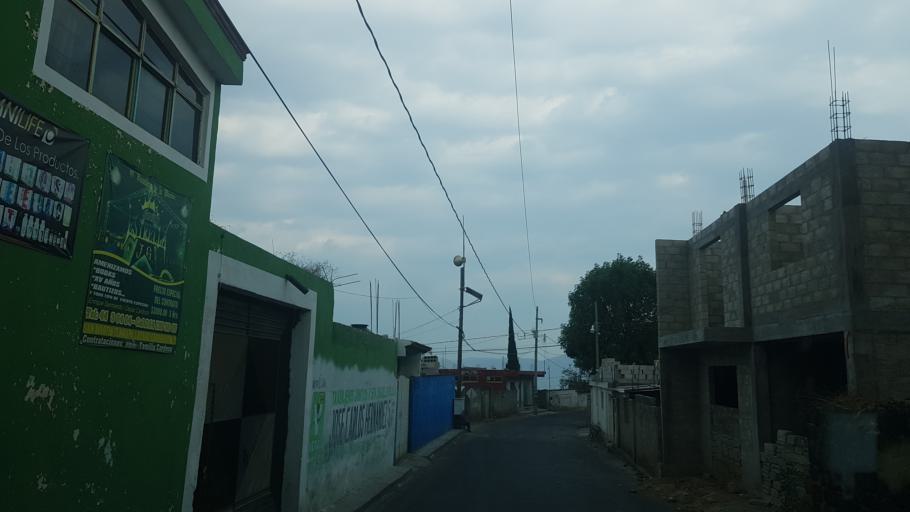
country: MX
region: Puebla
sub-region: Santa Isabel Cholula
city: San Martin Tlamapa
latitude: 18.9797
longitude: -98.3966
